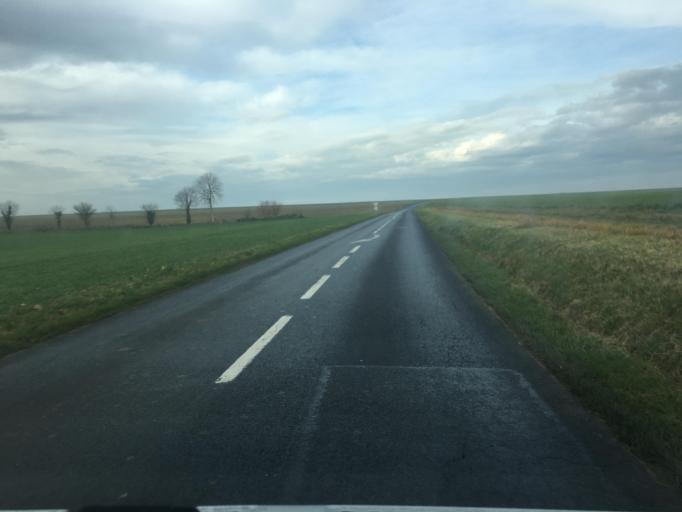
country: FR
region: Lower Normandy
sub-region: Departement du Calvados
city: Creully
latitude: 49.2938
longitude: -0.5438
